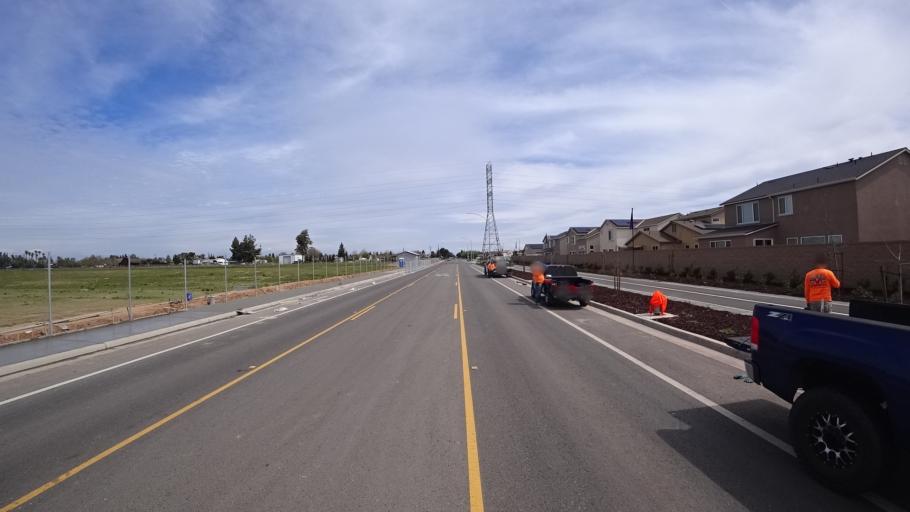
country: US
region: California
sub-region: Fresno County
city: West Park
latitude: 36.8007
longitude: -119.9020
